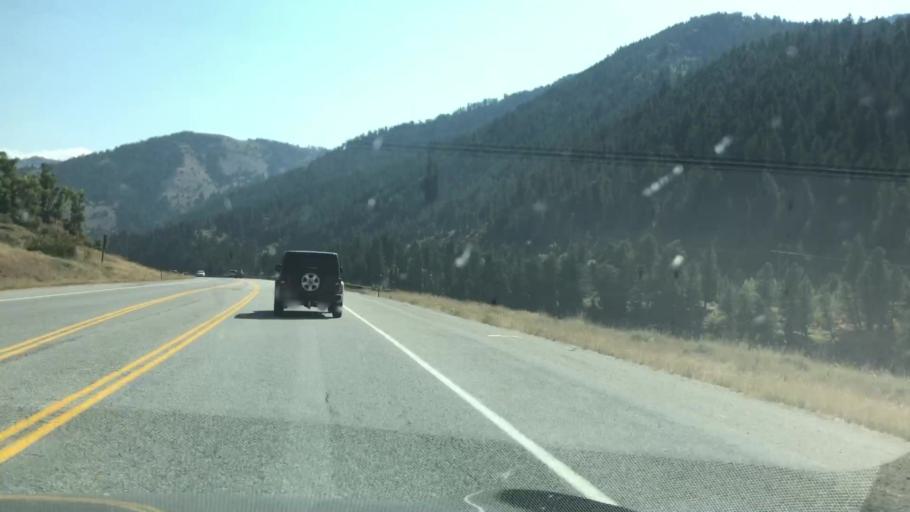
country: US
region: Wyoming
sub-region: Teton County
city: Hoback
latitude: 43.3007
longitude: -110.7696
